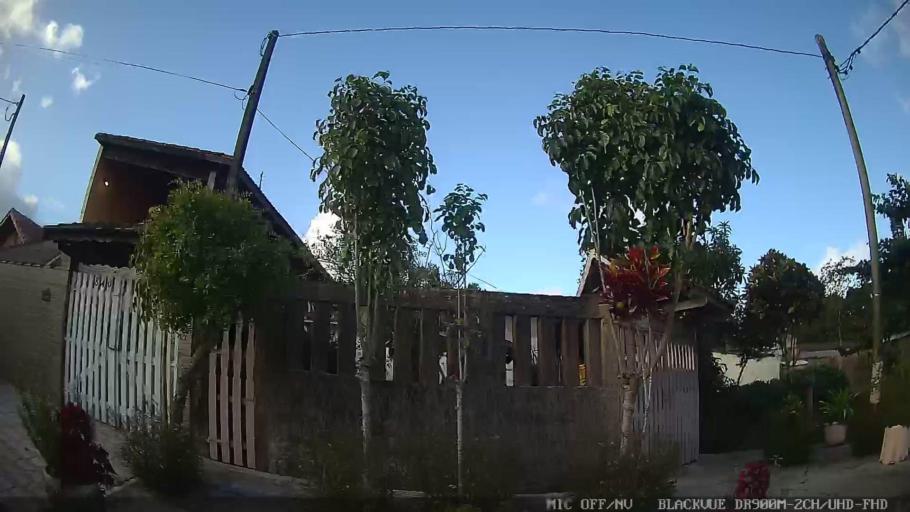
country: BR
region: Sao Paulo
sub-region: Itanhaem
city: Itanhaem
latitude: -24.1393
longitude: -46.7190
